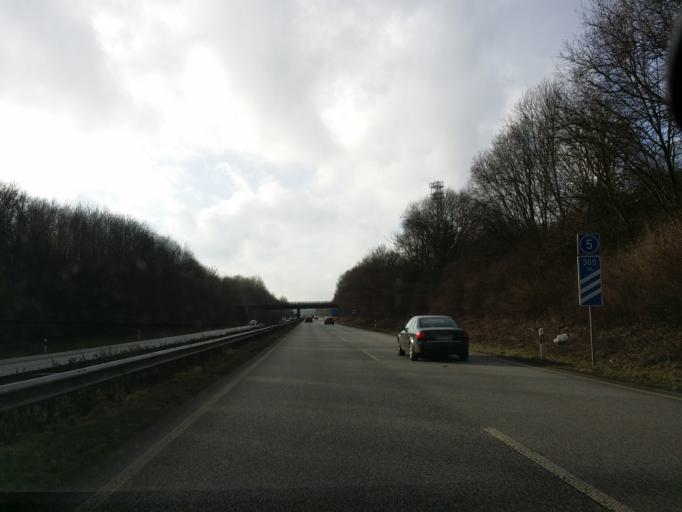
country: DE
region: Schleswig-Holstein
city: Achterwehr
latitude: 54.3199
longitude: 9.9525
